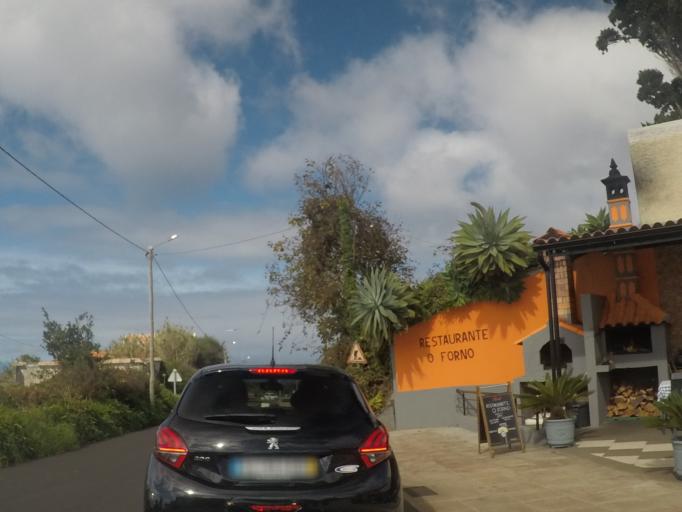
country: PT
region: Madeira
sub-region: Calheta
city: Faja da Ovelha
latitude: 32.8122
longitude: -17.2449
